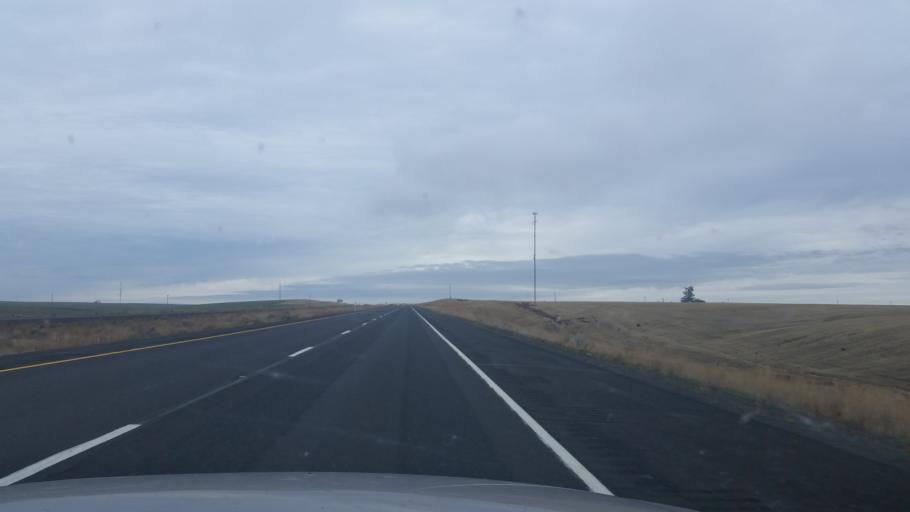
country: US
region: Washington
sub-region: Adams County
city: Ritzville
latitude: 47.1113
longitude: -118.4431
